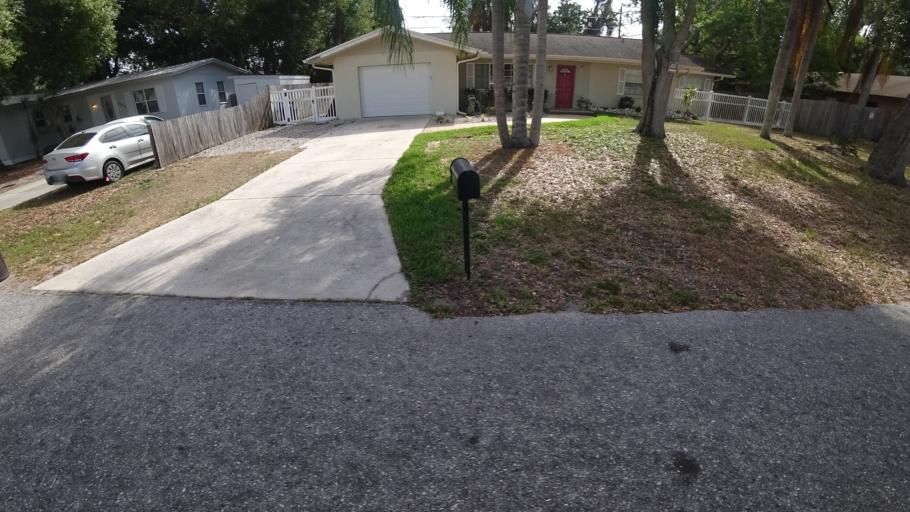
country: US
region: Florida
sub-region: Manatee County
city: Whitfield
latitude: 27.4243
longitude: -82.5636
